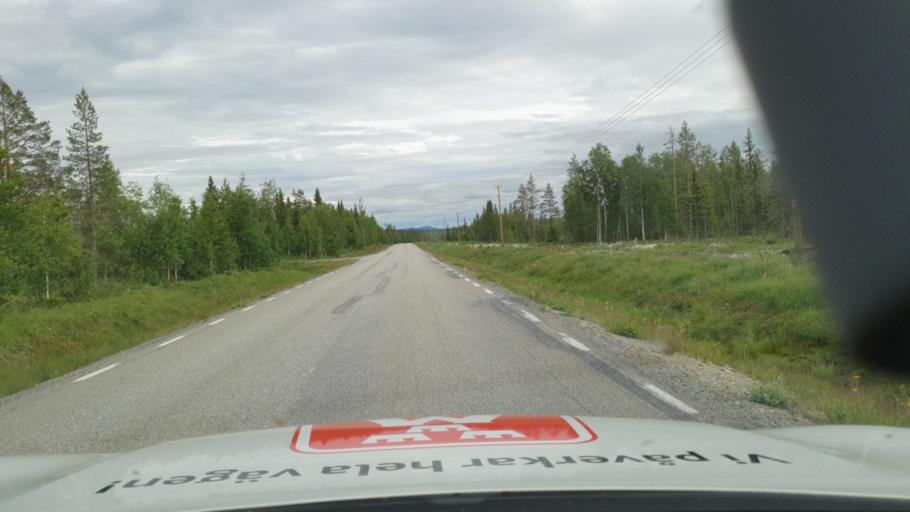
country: SE
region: Vaesterbotten
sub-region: Lycksele Kommun
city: Soderfors
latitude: 64.3806
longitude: 18.0253
